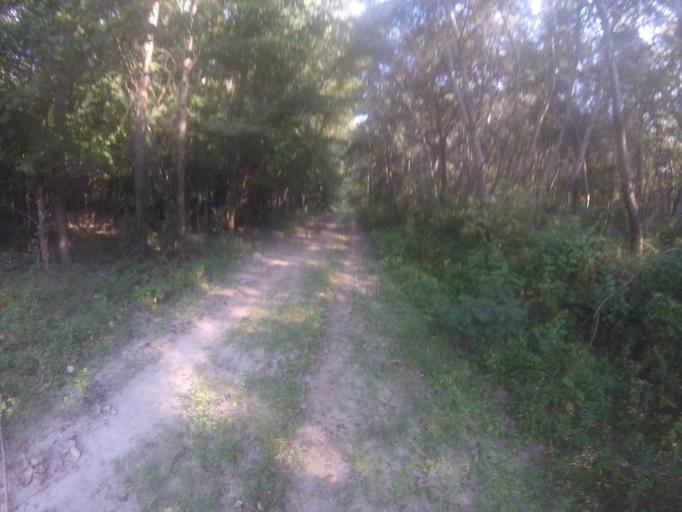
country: HU
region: Bacs-Kiskun
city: Baja
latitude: 46.1852
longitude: 18.9178
